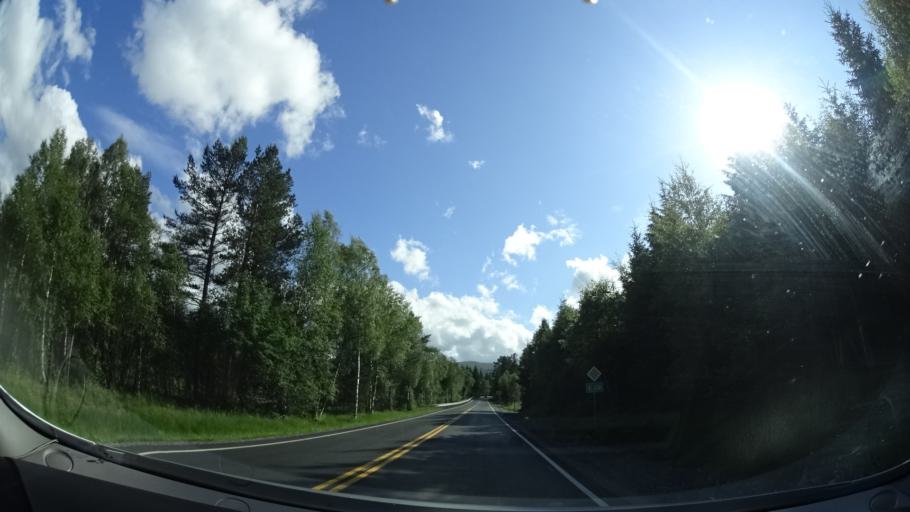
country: NO
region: Sor-Trondelag
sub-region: Hemne
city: Kyrksaeterora
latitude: 63.2112
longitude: 9.0205
